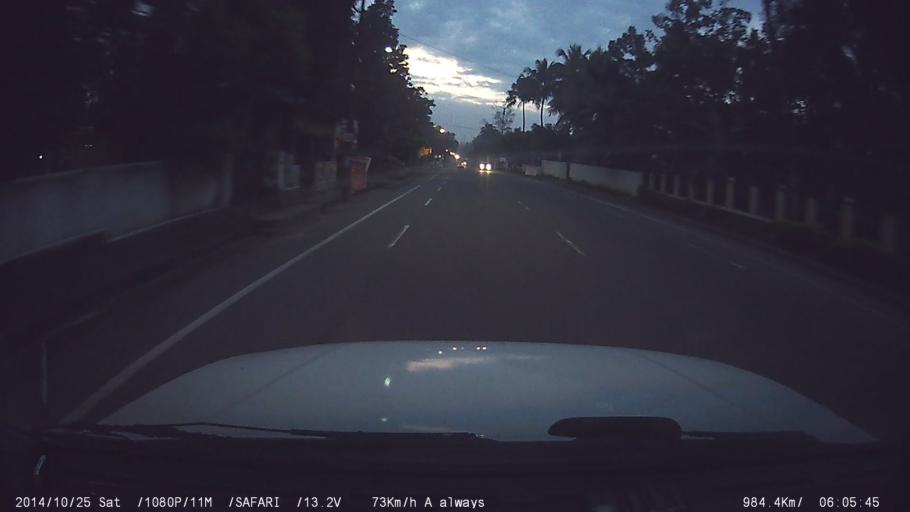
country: IN
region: Kerala
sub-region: Ernakulam
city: Angamali
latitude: 10.1818
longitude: 76.4122
